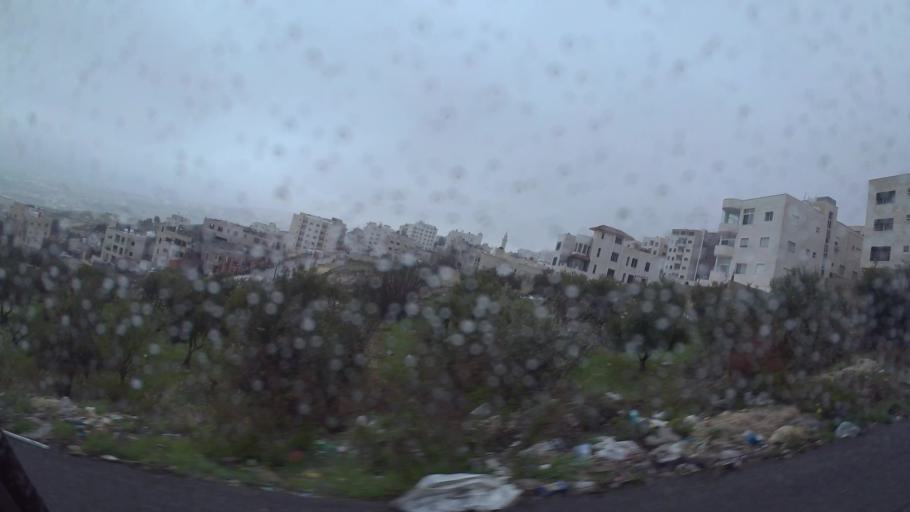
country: JO
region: Amman
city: Al Jubayhah
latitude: 32.0345
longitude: 35.8498
